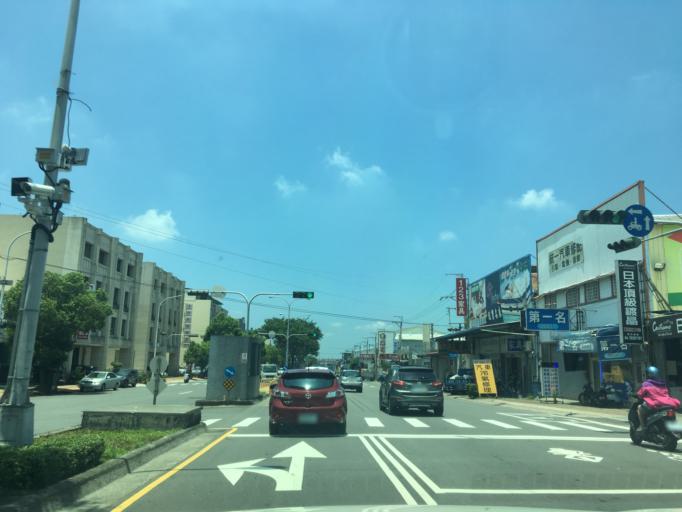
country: TW
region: Taiwan
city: Fengyuan
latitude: 24.2641
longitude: 120.7176
